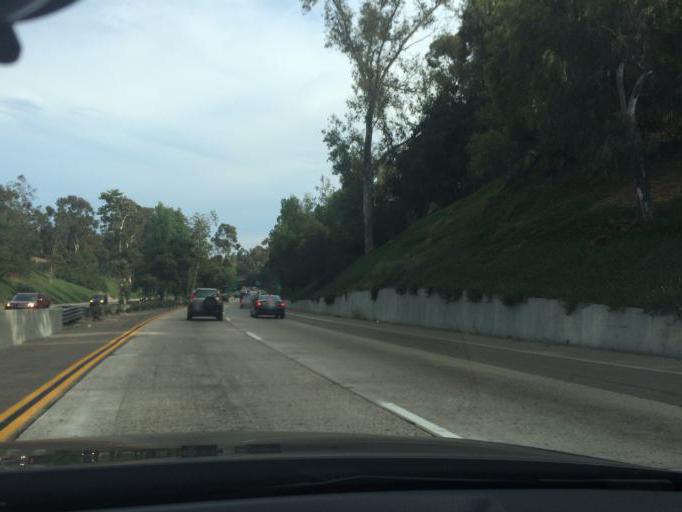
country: US
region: California
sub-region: San Diego County
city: San Diego
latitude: 32.7447
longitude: -117.1564
